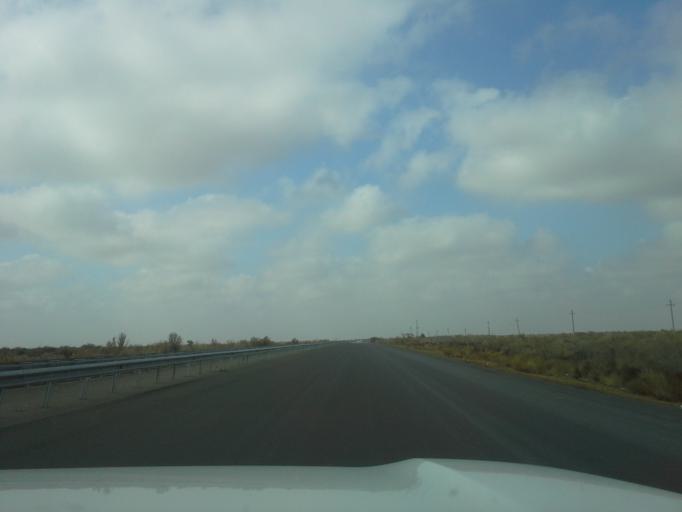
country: TM
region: Mary
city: Mary
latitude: 37.4187
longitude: 61.5659
